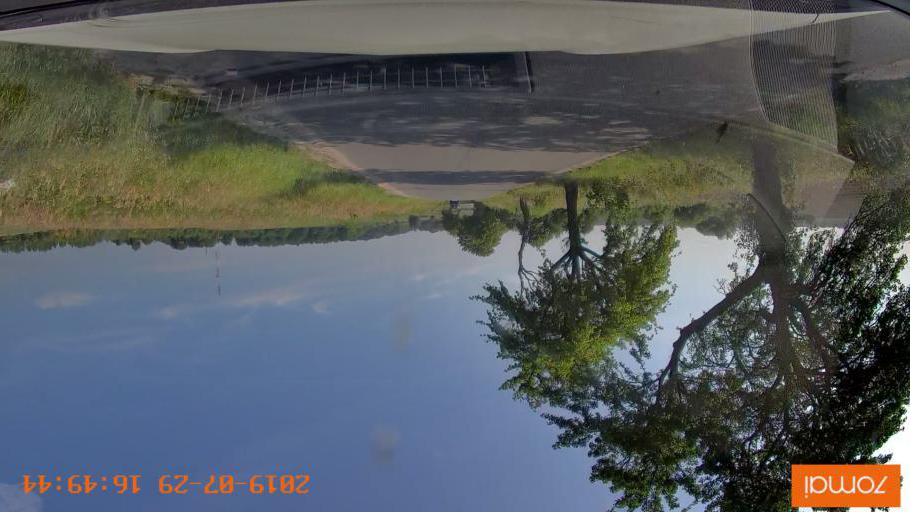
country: RU
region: Kaliningrad
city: Primorsk
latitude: 54.7969
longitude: 20.0620
